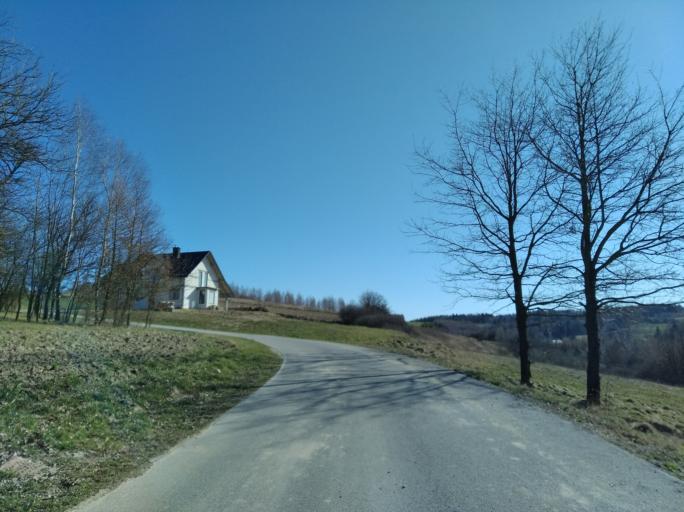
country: PL
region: Subcarpathian Voivodeship
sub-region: Powiat strzyzowski
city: Wisniowa
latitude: 49.9074
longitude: 21.6978
